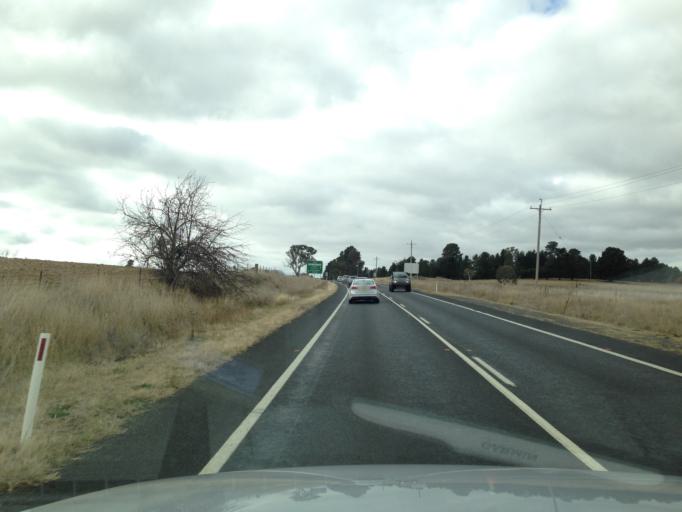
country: AU
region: New South Wales
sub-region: Cooma-Monaro
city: Cooma
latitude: -36.2488
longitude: 149.0469
